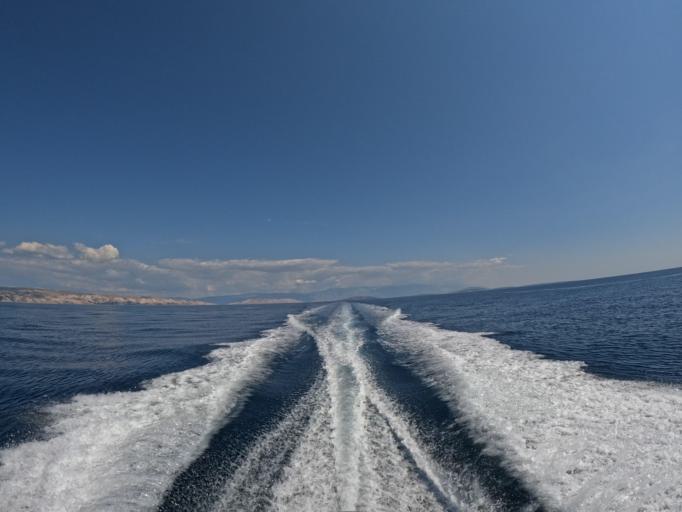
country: HR
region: Primorsko-Goranska
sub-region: Grad Krk
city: Krk
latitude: 44.9230
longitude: 14.5531
